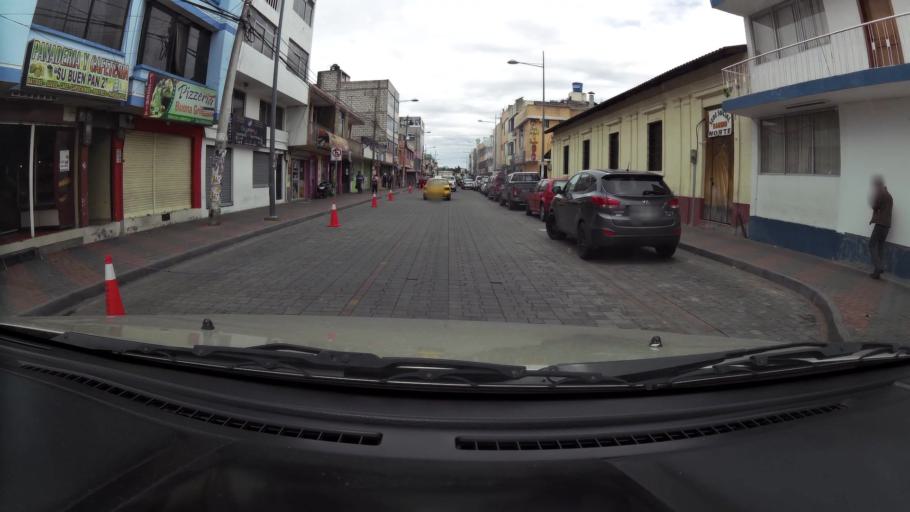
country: EC
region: Cotopaxi
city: San Miguel de Salcedo
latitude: -1.0241
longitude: -78.5915
